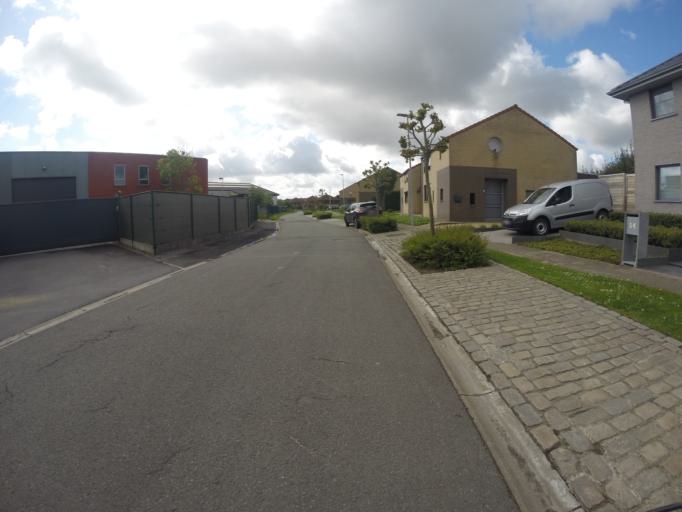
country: BE
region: Flanders
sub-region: Provincie West-Vlaanderen
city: Ruiselede
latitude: 51.0448
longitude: 3.4065
